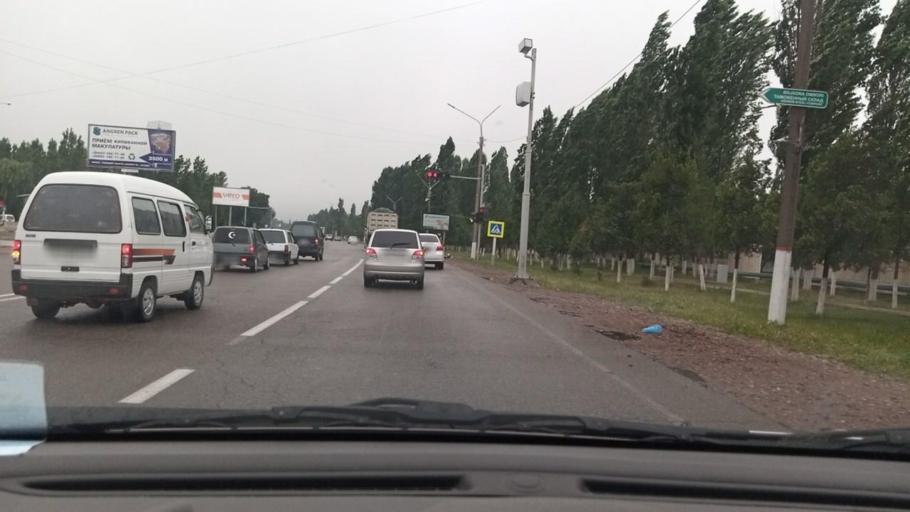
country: UZ
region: Toshkent
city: Angren
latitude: 40.9918
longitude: 70.0444
